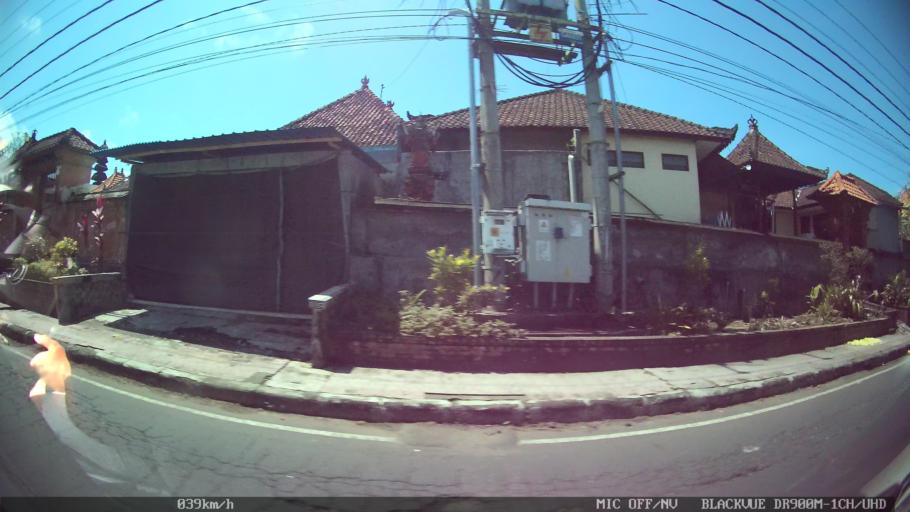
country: ID
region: Bali
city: Klungkung
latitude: -8.5644
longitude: 115.3416
